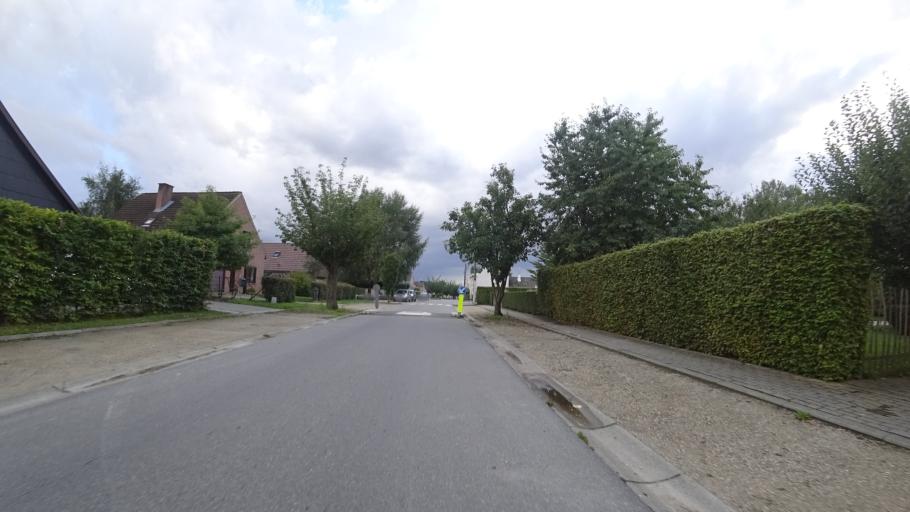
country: BE
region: Wallonia
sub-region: Province du Brabant Wallon
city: Chastre-Villeroux-Blanmont
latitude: 50.6366
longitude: 4.6541
